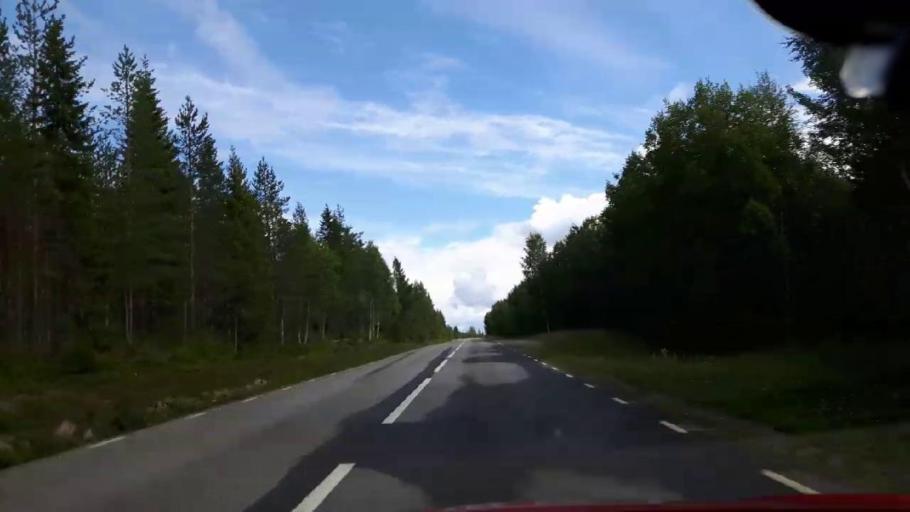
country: SE
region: Jaemtland
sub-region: Stroemsunds Kommun
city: Stroemsund
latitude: 64.3465
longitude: 15.0915
